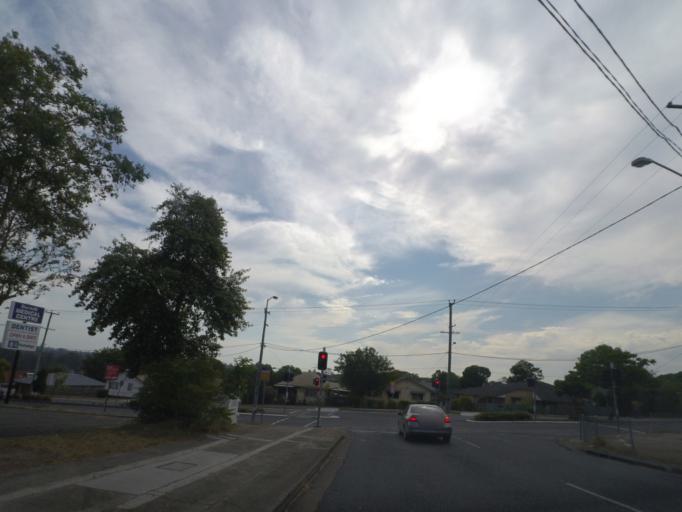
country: AU
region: Queensland
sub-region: Brisbane
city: Inala
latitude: -27.5870
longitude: 152.9765
